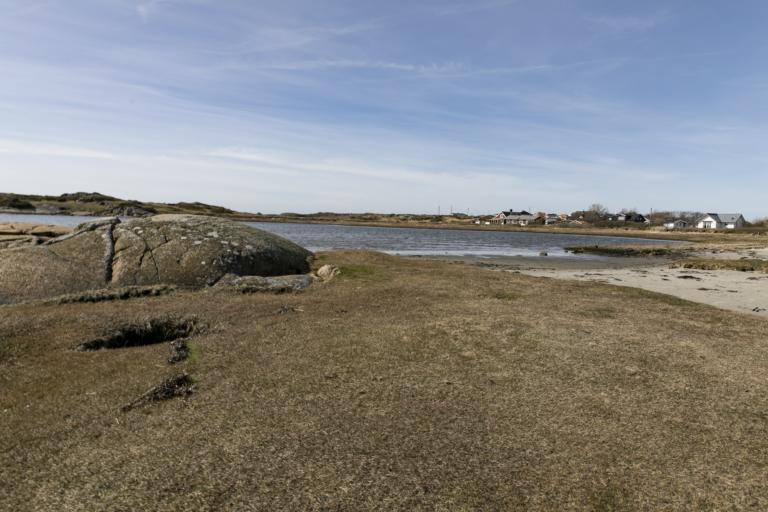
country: SE
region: Halland
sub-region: Varbergs Kommun
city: Varberg
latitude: 57.1132
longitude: 12.2177
